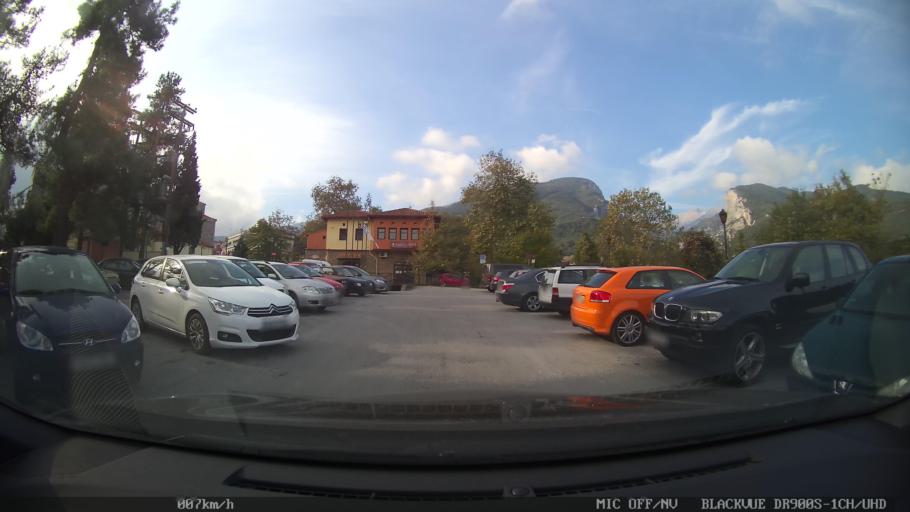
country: GR
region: Central Macedonia
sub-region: Nomos Pierias
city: Litochoro
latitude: 40.1054
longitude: 22.5019
